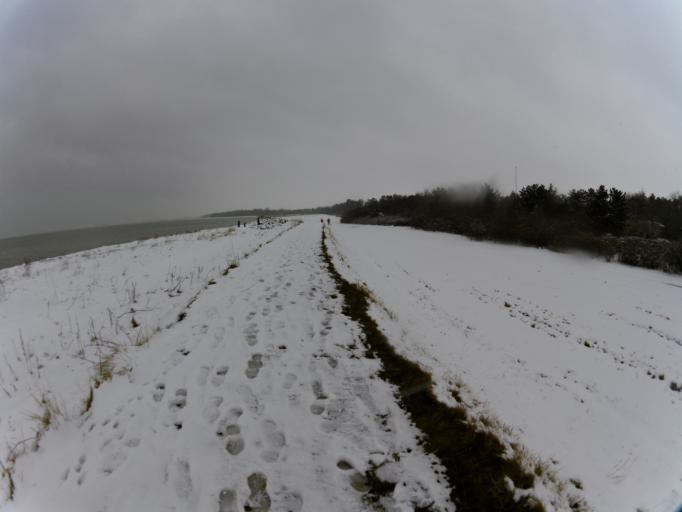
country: DK
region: Zealand
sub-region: Vordingborg Kommune
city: Neder Vindinge
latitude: 55.0483
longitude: 11.8330
